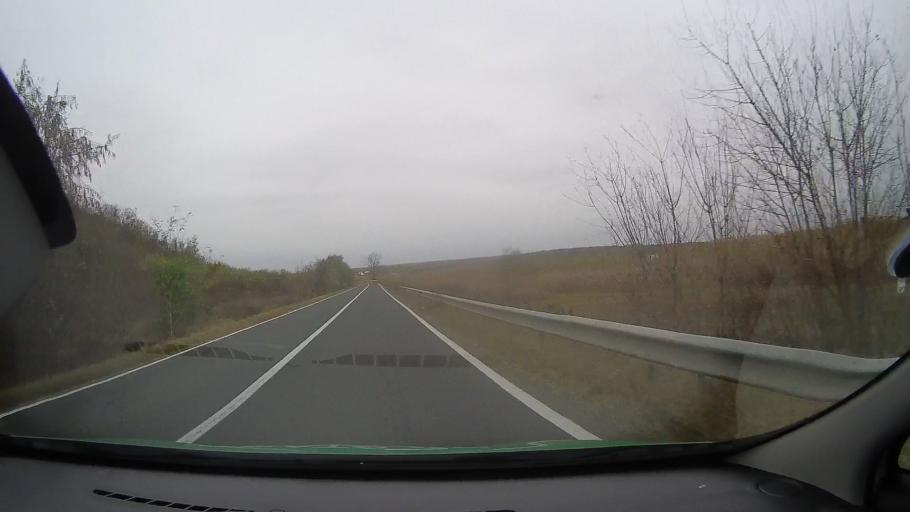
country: RO
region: Constanta
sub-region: Comuna Garliciu
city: Garliciu
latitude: 44.7075
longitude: 28.0657
